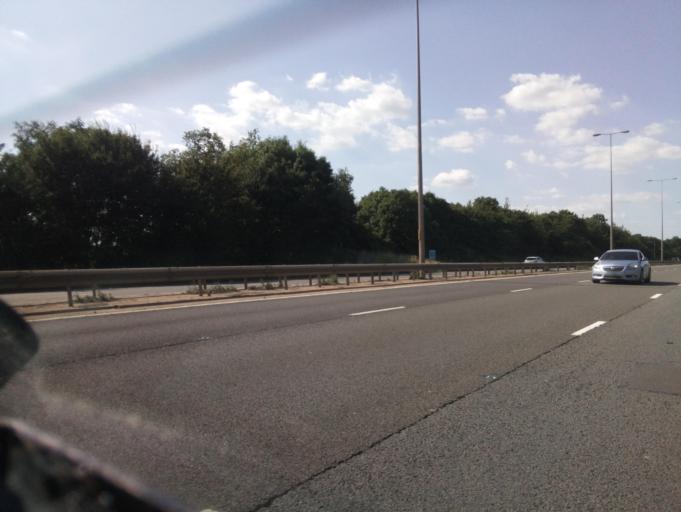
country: GB
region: England
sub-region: Worcestershire
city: Kempsey
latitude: 52.1136
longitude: -2.1959
